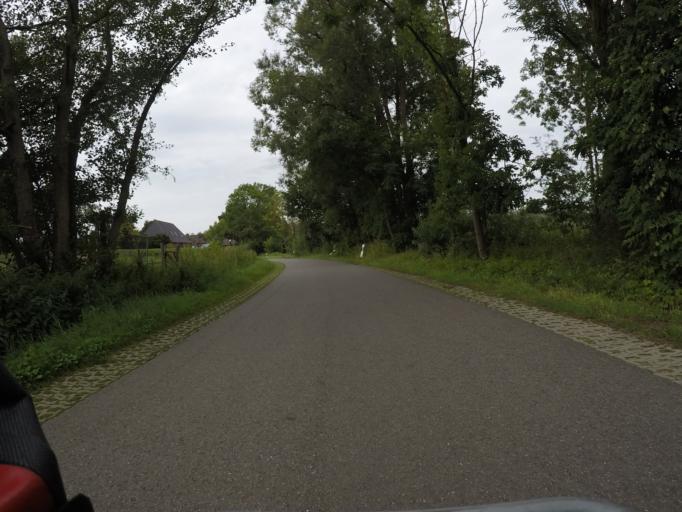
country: DE
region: Lower Saxony
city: Winsen
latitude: 53.3831
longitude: 10.2029
